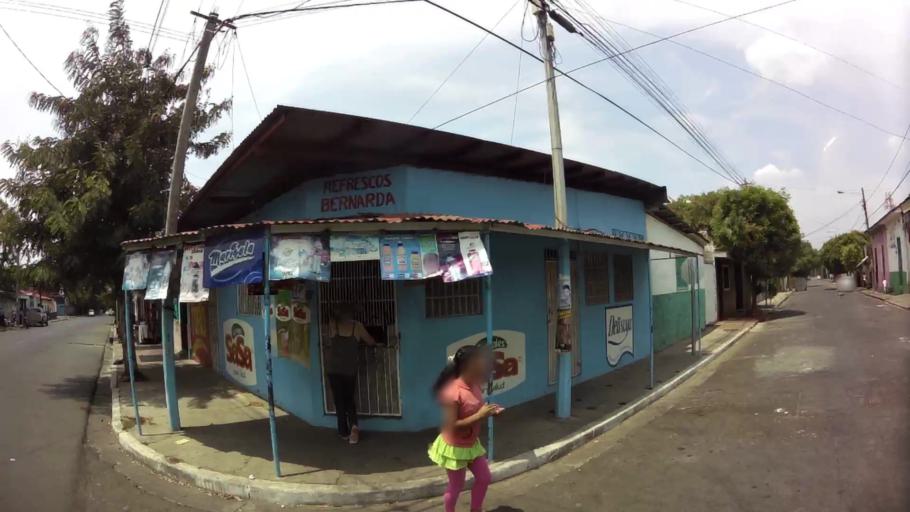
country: NI
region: Managua
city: Managua
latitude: 12.1505
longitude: -86.2888
